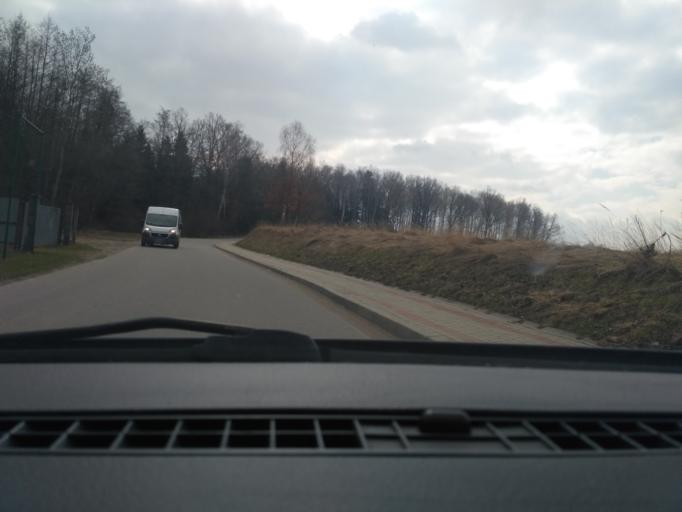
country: PL
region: Subcarpathian Voivodeship
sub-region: Powiat krosnienski
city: Kroscienko Wyzne
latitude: 49.6699
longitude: 21.8297
